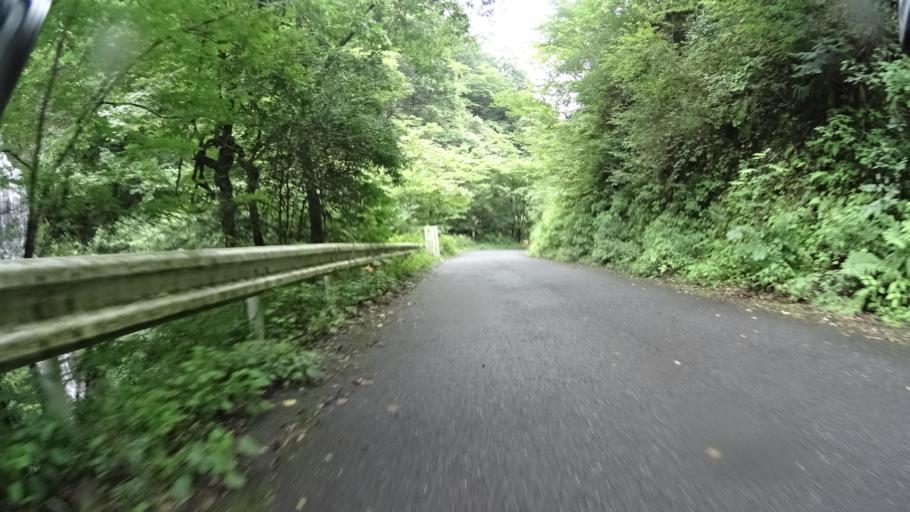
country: JP
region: Saitama
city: Chichibu
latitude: 35.8791
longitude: 139.1454
